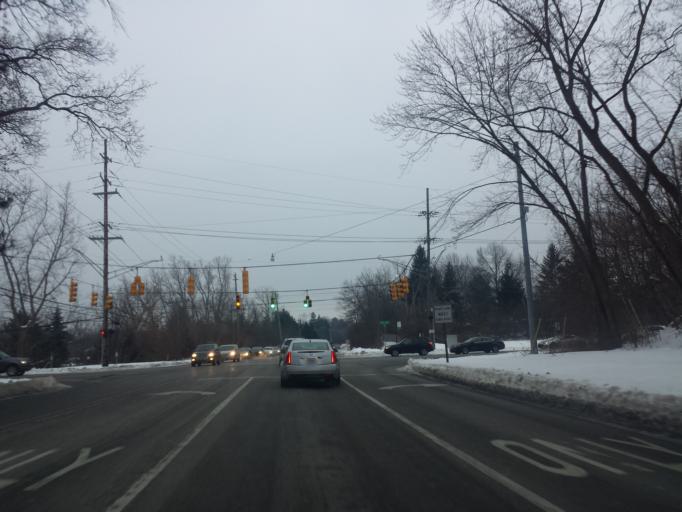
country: US
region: Michigan
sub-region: Oakland County
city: Sylvan Lake
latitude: 42.5861
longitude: -83.3298
